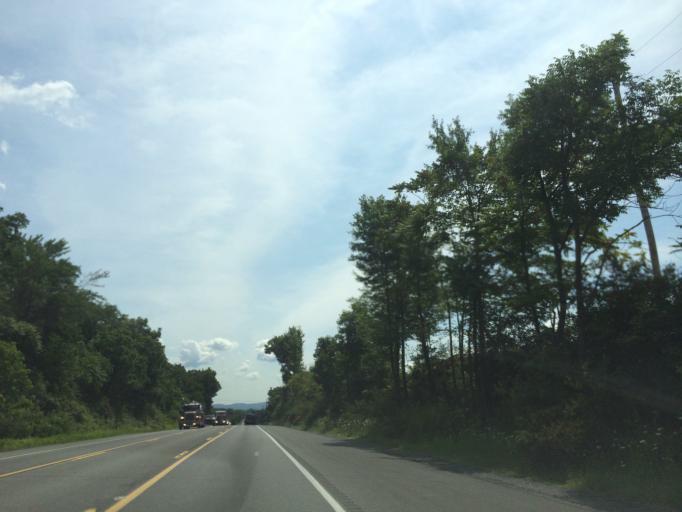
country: US
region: Pennsylvania
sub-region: Lehigh County
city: Breinigsville
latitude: 40.5422
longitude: -75.6526
